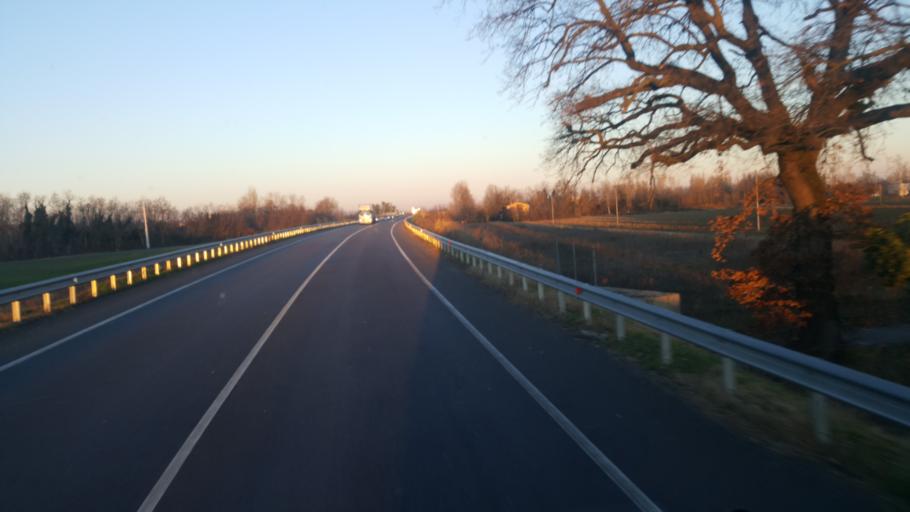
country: IT
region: Emilia-Romagna
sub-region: Provincia di Bologna
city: Bazzano
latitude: 44.5129
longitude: 11.0855
